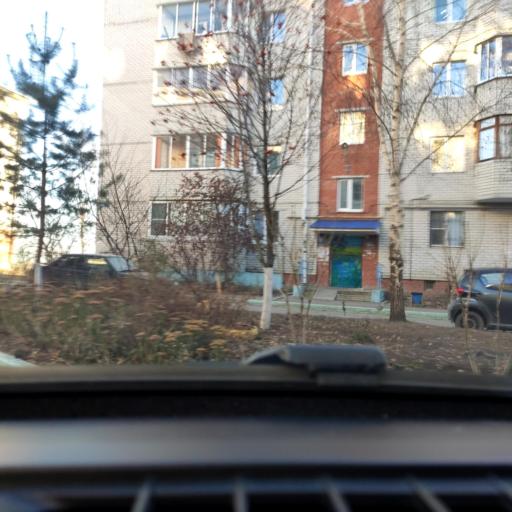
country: RU
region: Voronezj
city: Novaya Usman'
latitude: 51.6054
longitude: 39.3892
